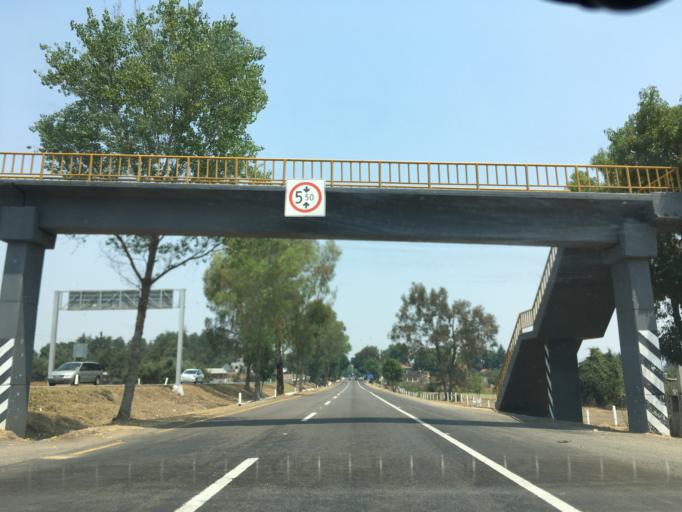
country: MX
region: Michoacan
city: Patzcuaro
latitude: 19.5319
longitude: -101.5647
